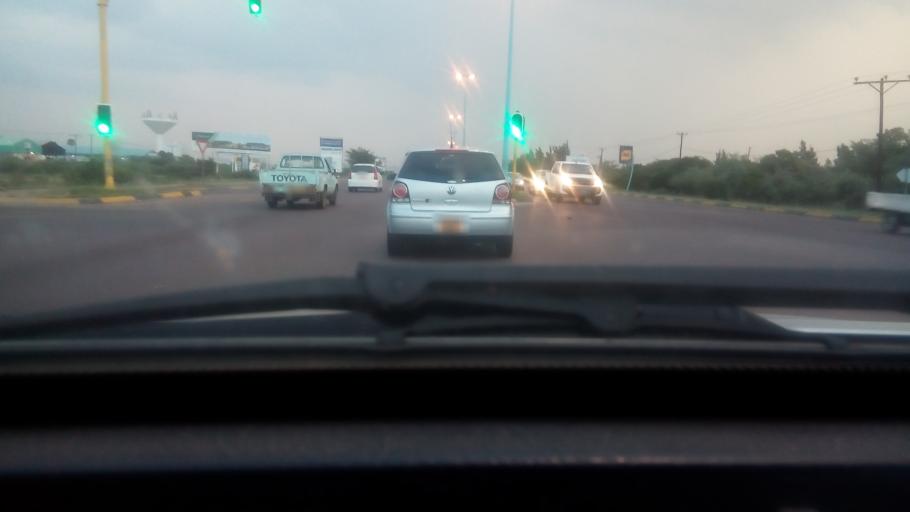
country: BW
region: Kweneng
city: Mmopone
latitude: -24.5610
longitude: 25.9746
